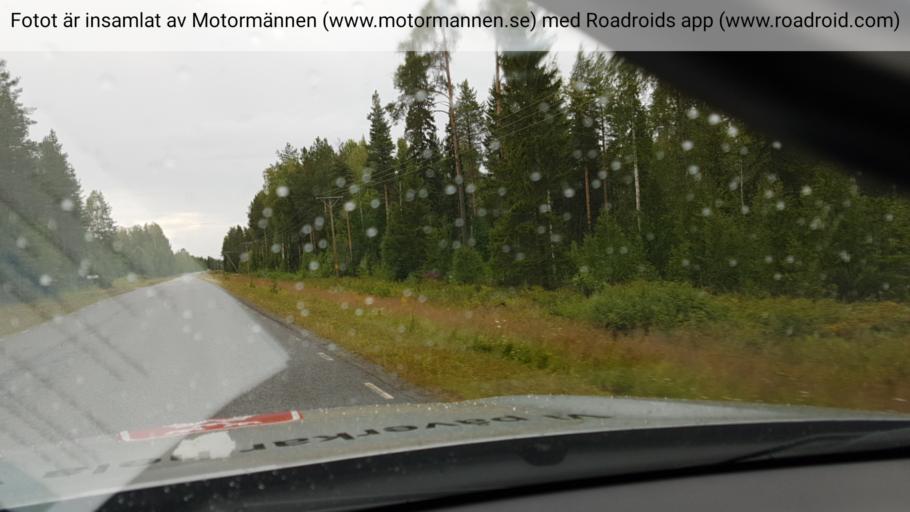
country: SE
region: Norrbotten
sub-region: Bodens Kommun
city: Boden
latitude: 65.8306
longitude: 21.5060
